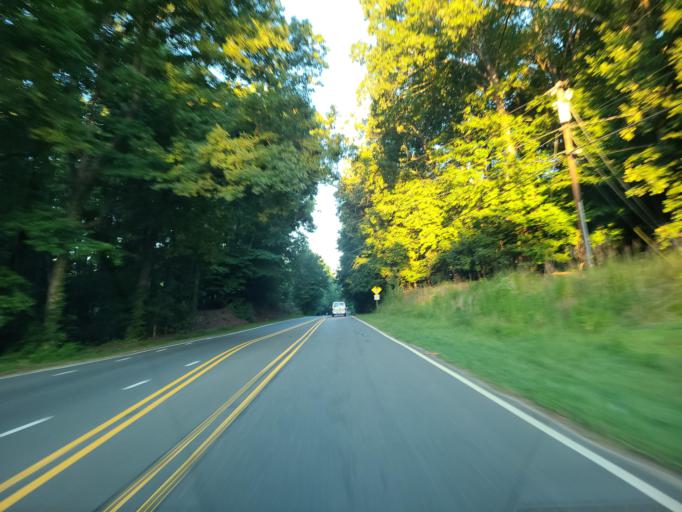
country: US
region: North Carolina
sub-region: Union County
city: Wesley Chapel
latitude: 35.0007
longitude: -80.7197
